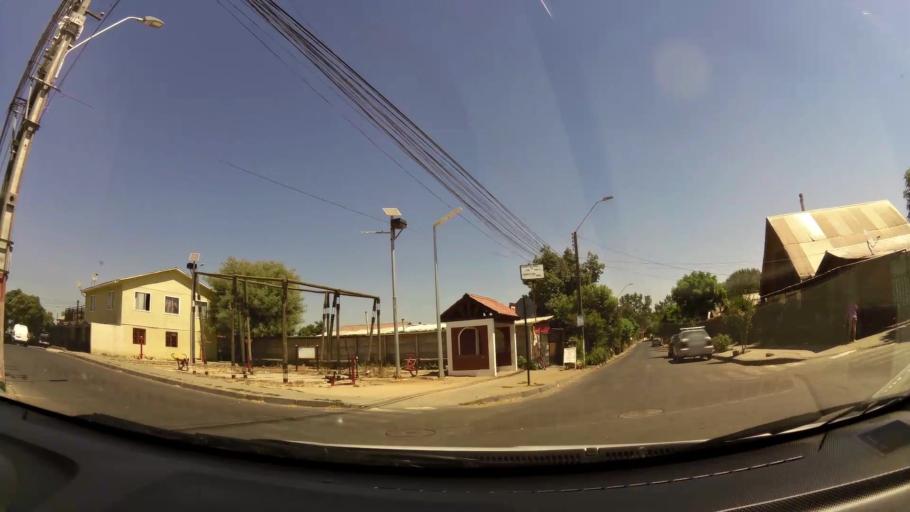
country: CL
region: Maule
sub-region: Provincia de Talca
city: Talca
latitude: -35.3063
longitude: -71.5135
